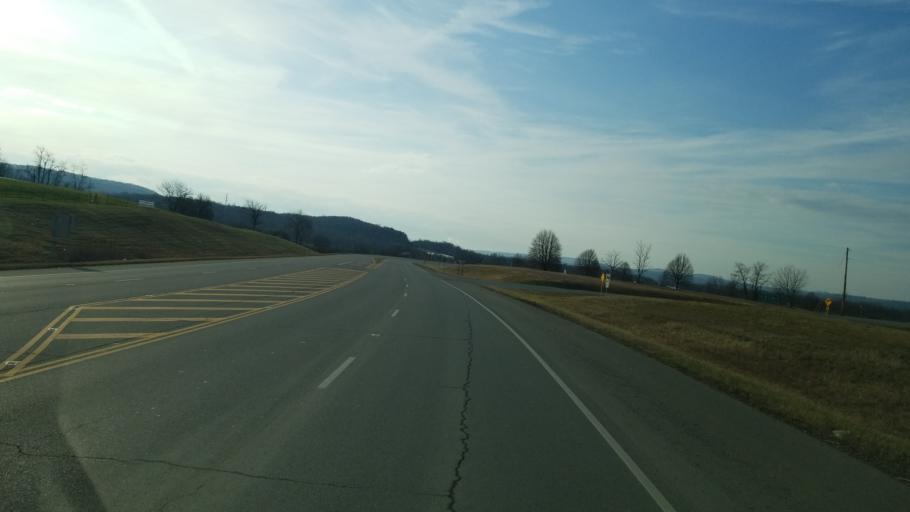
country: US
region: Ohio
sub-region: Ross County
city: Chillicothe
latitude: 39.3930
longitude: -82.9680
